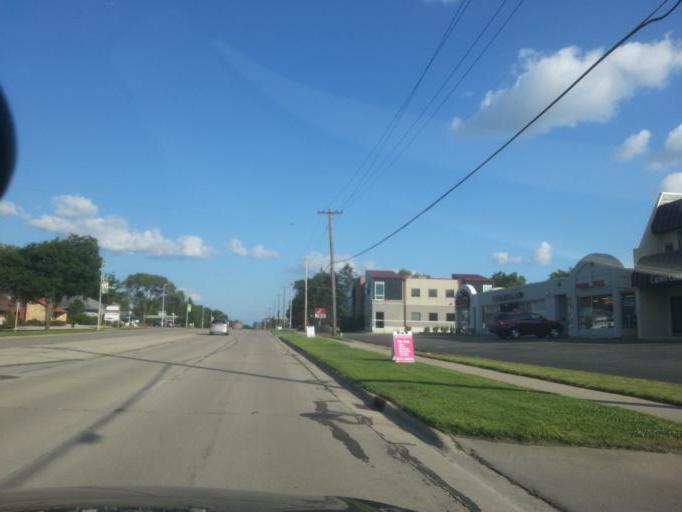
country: US
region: Wisconsin
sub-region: Dane County
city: Middleton
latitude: 43.0960
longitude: -89.4952
